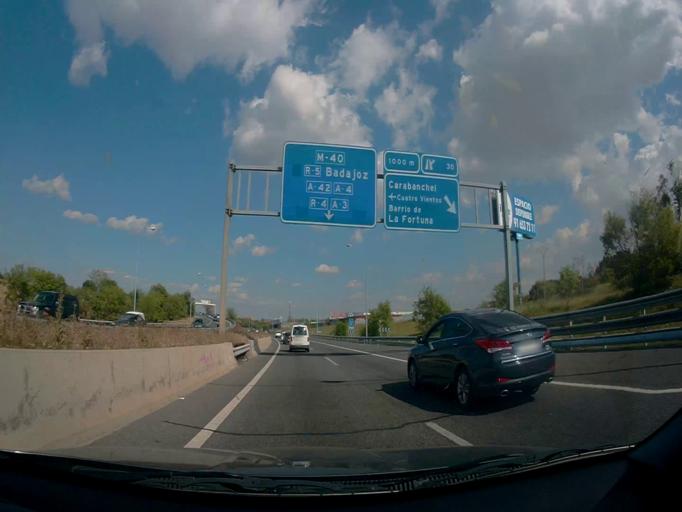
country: ES
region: Madrid
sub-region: Provincia de Madrid
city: Alcorcon
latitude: 40.3612
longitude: -3.7928
